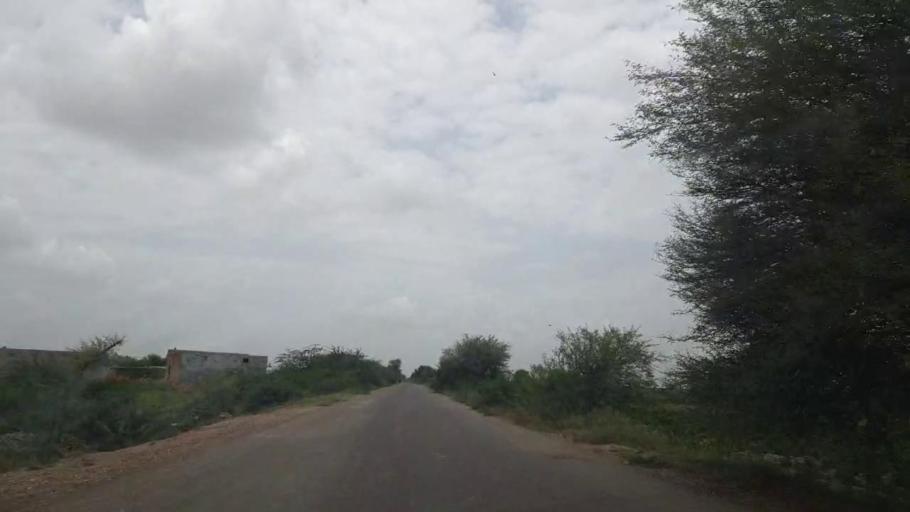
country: PK
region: Sindh
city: Naukot
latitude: 24.8974
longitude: 69.2579
